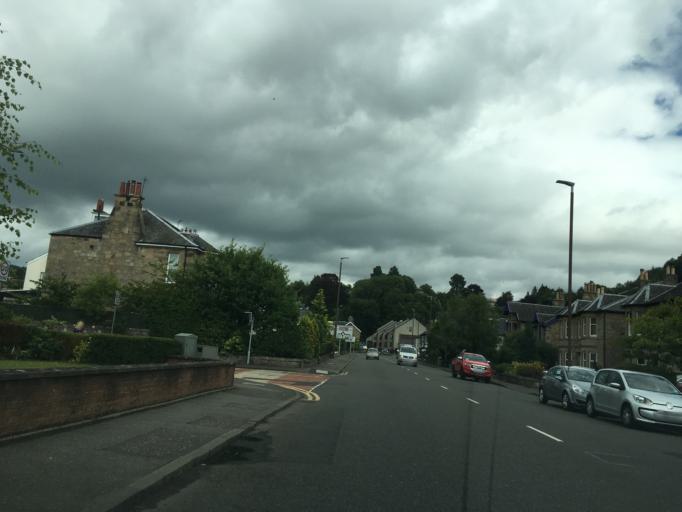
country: GB
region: Scotland
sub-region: Stirling
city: Stirling
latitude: 56.1372
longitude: -3.9251
